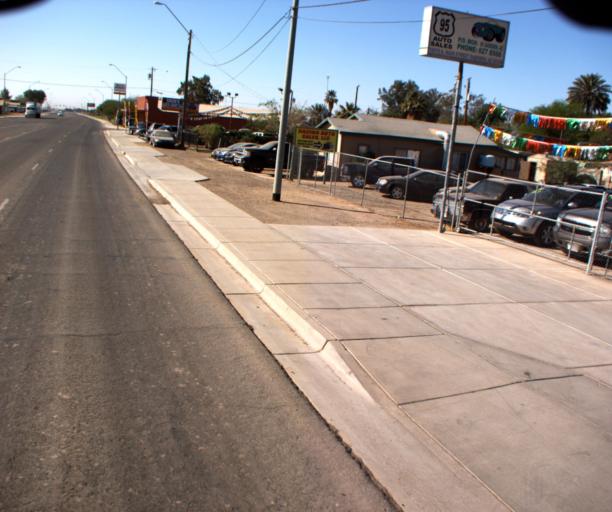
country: US
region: Arizona
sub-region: Yuma County
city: San Luis
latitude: 32.5584
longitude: -114.7848
